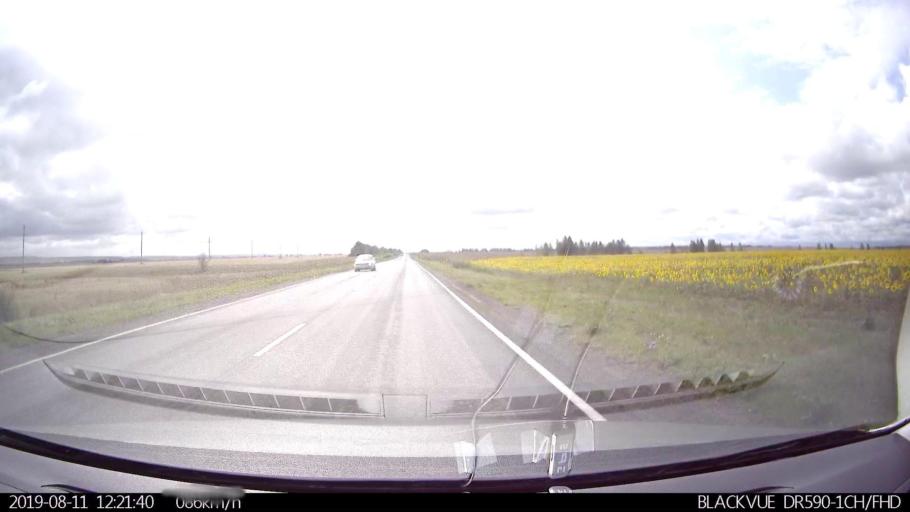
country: RU
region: Ulyanovsk
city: Ignatovka
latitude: 53.9182
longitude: 47.9571
